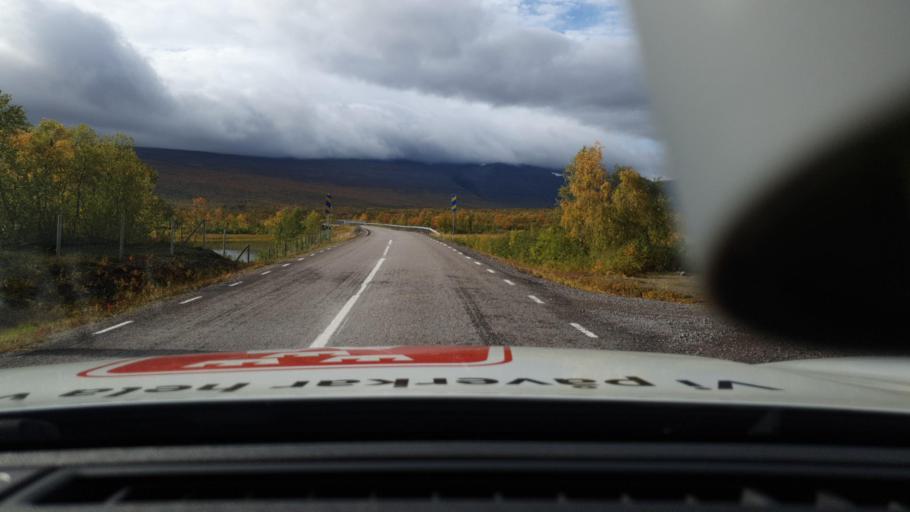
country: SE
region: Norrbotten
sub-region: Kiruna Kommun
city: Kiruna
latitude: 67.8622
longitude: 19.0329
